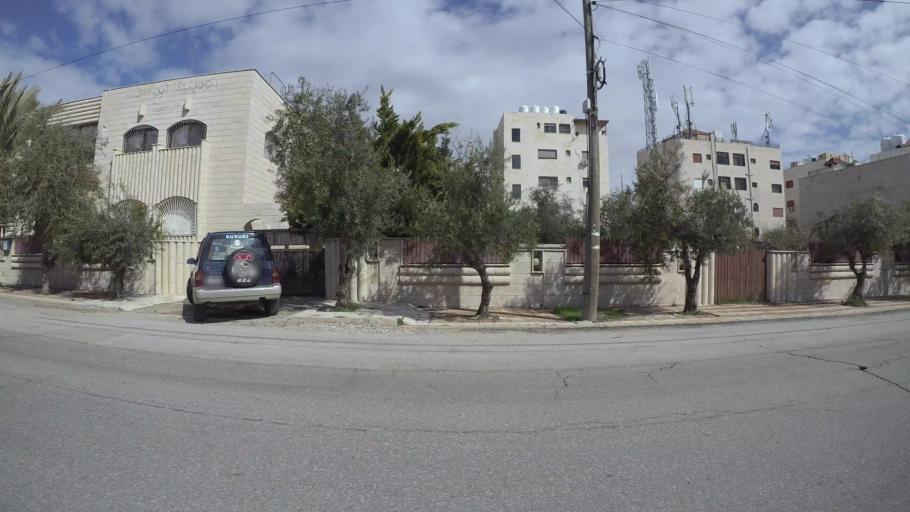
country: JO
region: Amman
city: Al Jubayhah
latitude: 32.0013
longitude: 35.8385
